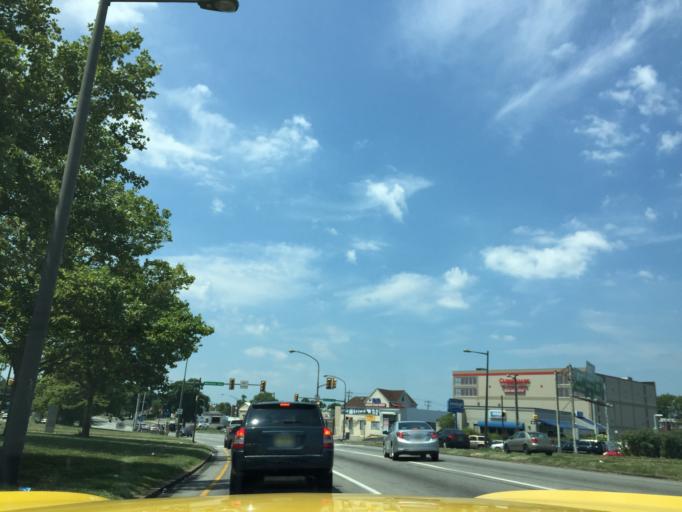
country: US
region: Pennsylvania
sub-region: Montgomery County
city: Rockledge
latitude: 40.0299
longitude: -75.1033
